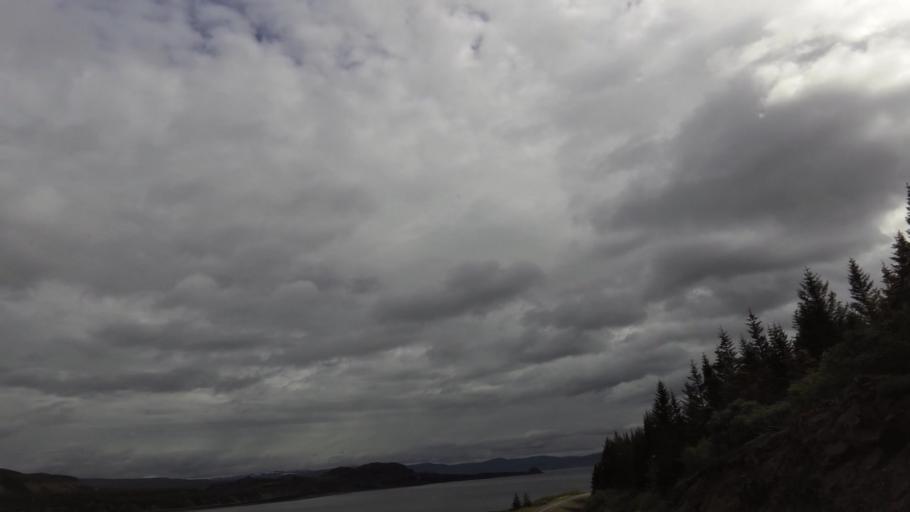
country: IS
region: West
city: Stykkisholmur
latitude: 65.5175
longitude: -22.1130
